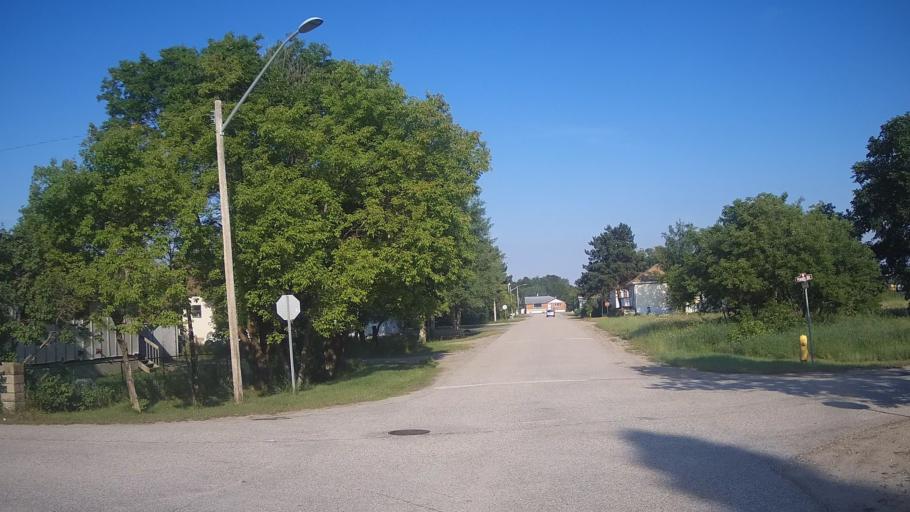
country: CA
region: Ontario
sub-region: Rainy River District
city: Atikokan
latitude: 49.4175
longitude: -91.6611
